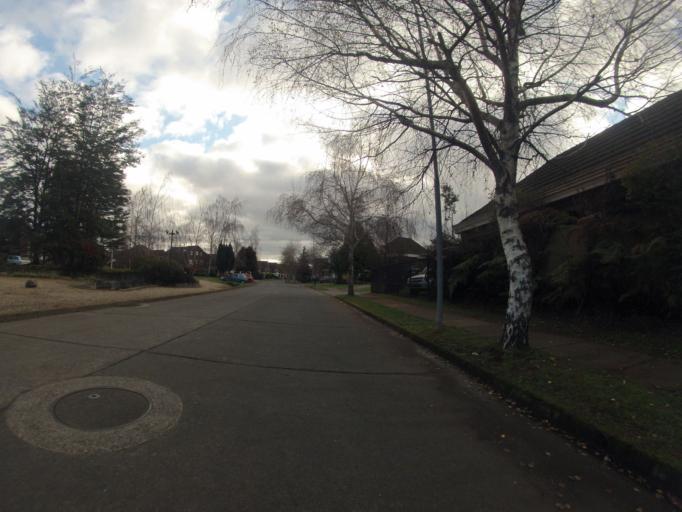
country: CL
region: Araucania
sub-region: Provincia de Cautin
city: Temuco
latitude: -38.7380
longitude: -72.6424
